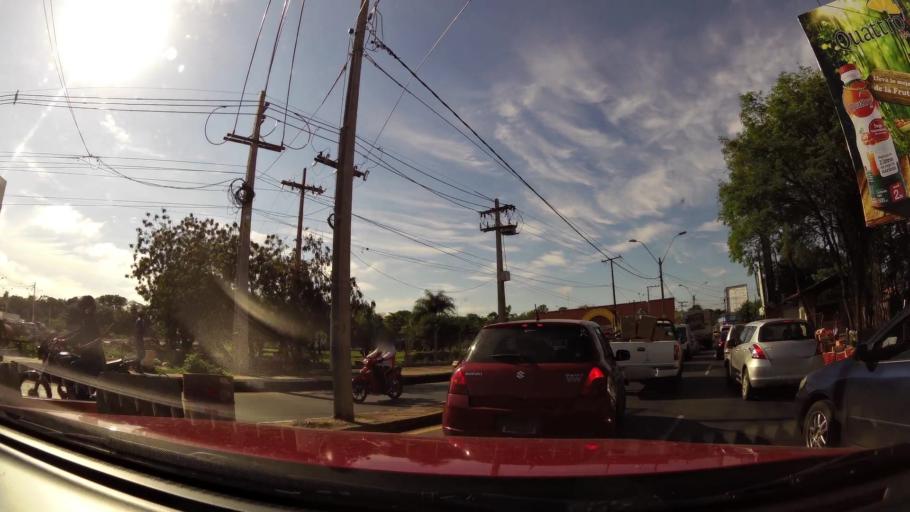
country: PY
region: Central
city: Fernando de la Mora
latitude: -25.2628
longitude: -57.5162
